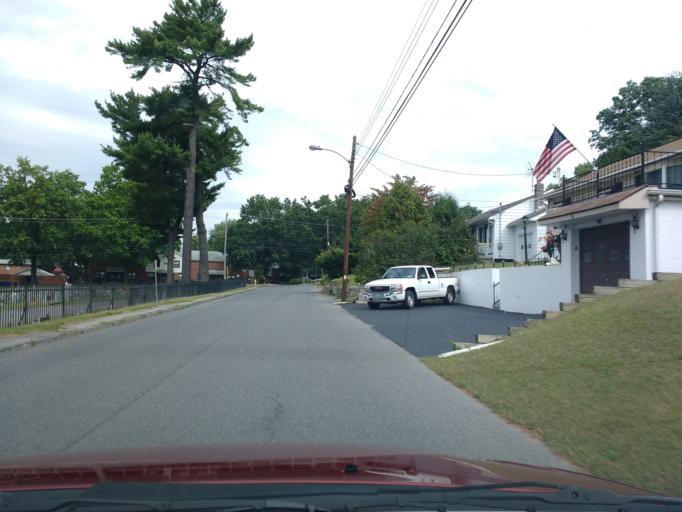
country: US
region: New York
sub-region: Ulster County
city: Kingston
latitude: 41.9378
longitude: -73.9924
